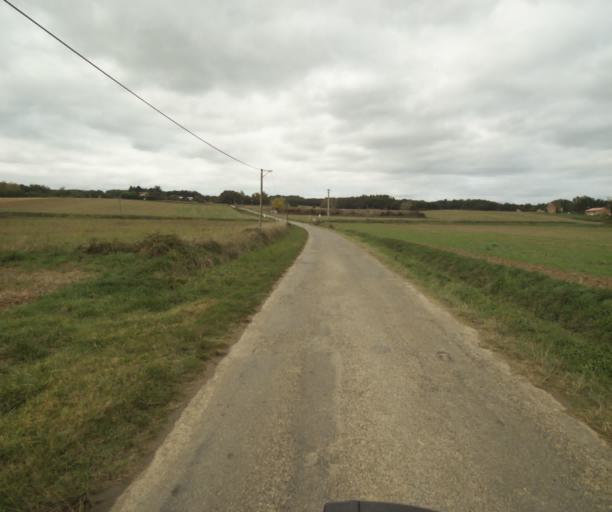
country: FR
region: Midi-Pyrenees
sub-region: Departement de la Haute-Garonne
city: Launac
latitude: 43.8398
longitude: 1.1097
